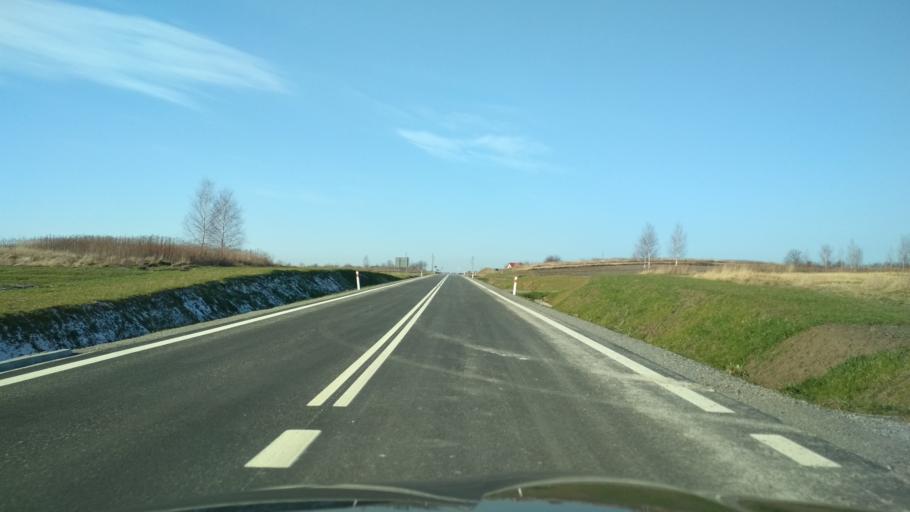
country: PL
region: Subcarpathian Voivodeship
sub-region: Powiat ropczycko-sedziszowski
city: Sedziszow Malopolski
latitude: 50.0739
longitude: 21.7303
